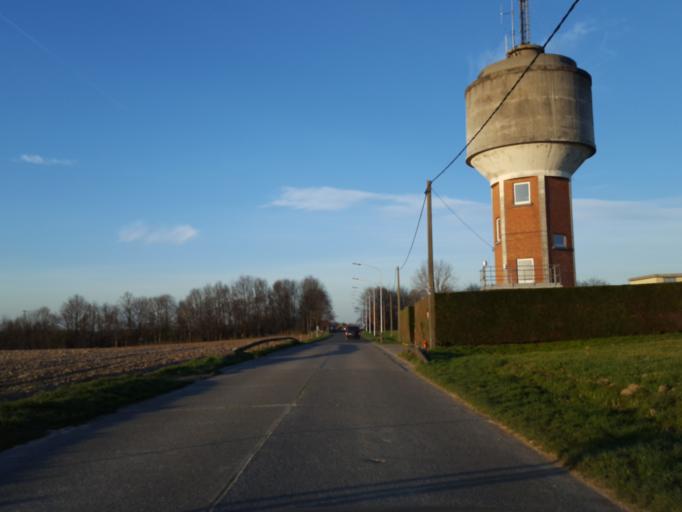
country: BE
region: Wallonia
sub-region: Province du Brabant Wallon
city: Walhain-Saint-Paul
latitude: 50.6551
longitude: 4.6681
